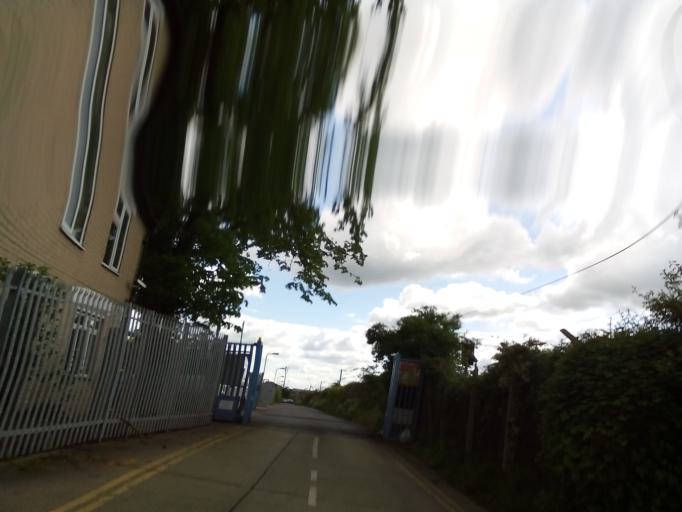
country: GB
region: England
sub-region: Cambridgeshire
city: Cambridge
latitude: 52.2103
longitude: 0.1497
